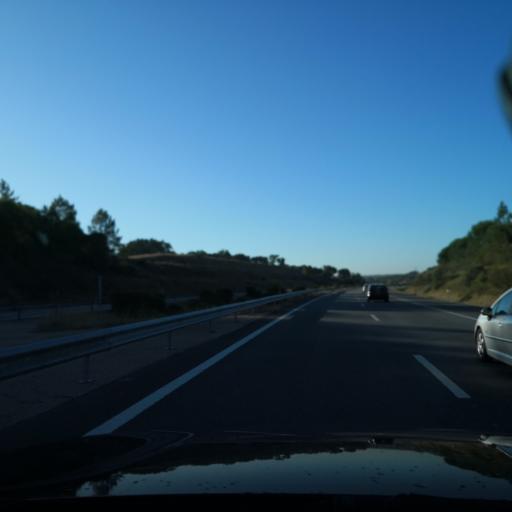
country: PT
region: Evora
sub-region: Vendas Novas
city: Vendas Novas
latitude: 38.5929
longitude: -8.6271
